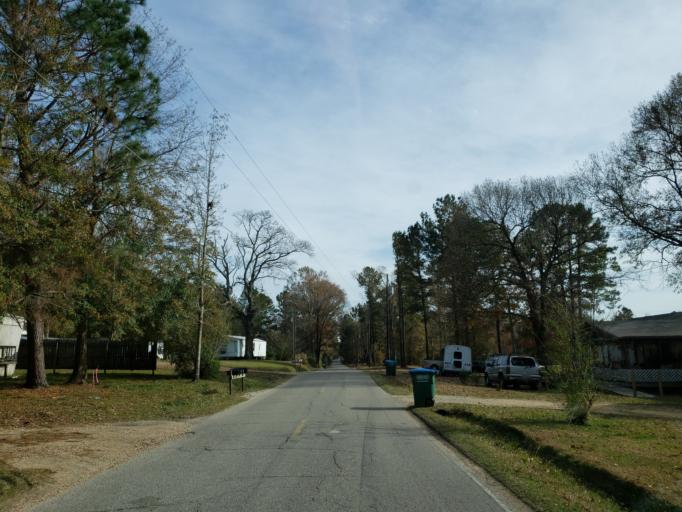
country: US
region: Mississippi
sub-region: Forrest County
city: Rawls Springs
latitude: 31.3967
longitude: -89.3889
